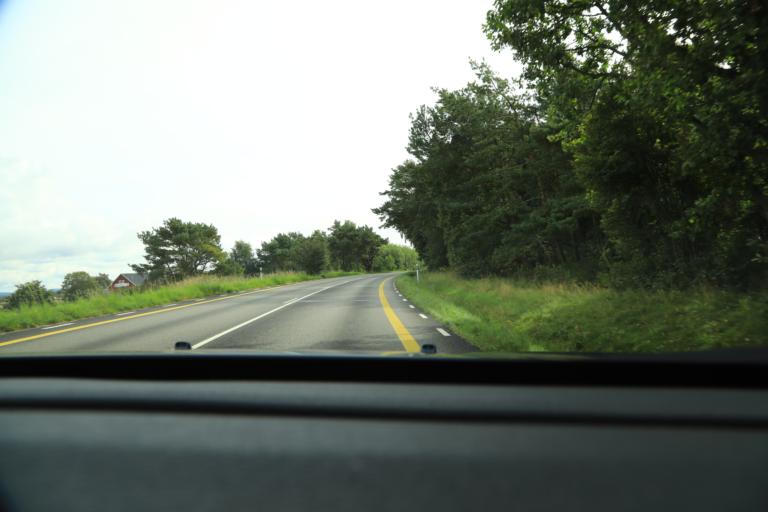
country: SE
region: Halland
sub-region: Varbergs Kommun
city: Traslovslage
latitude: 57.0415
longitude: 12.3216
